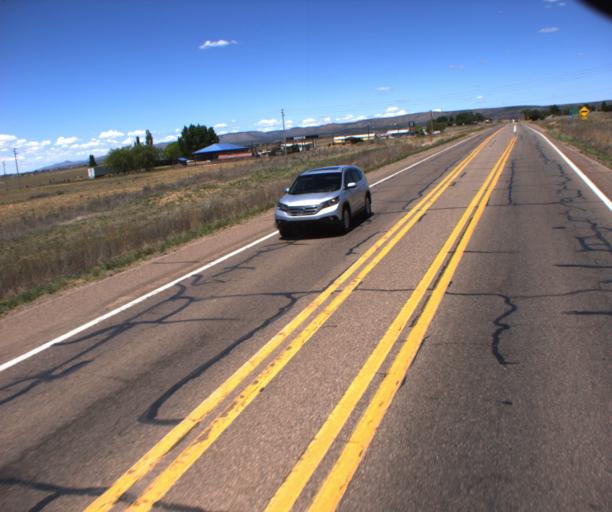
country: US
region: Arizona
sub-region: Yavapai County
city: Paulden
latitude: 34.8784
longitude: -112.4689
